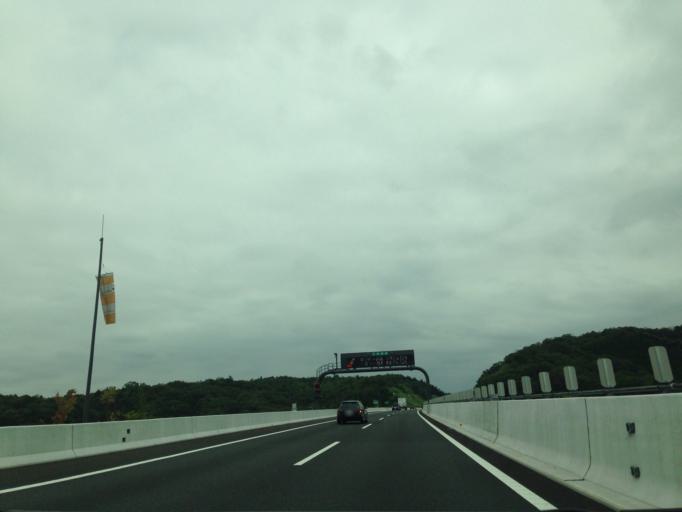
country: JP
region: Aichi
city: Okazaki
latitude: 34.9832
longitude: 137.2388
